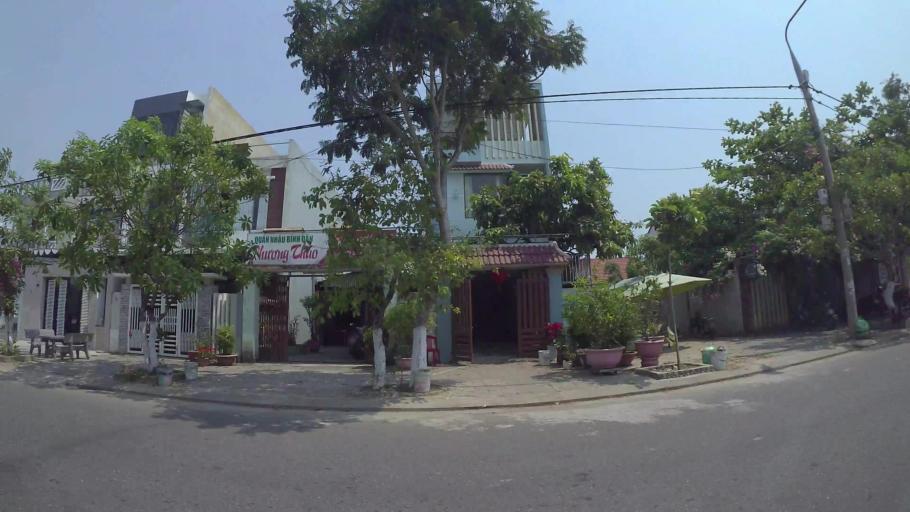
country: VN
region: Da Nang
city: Cam Le
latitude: 15.9997
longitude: 108.2027
